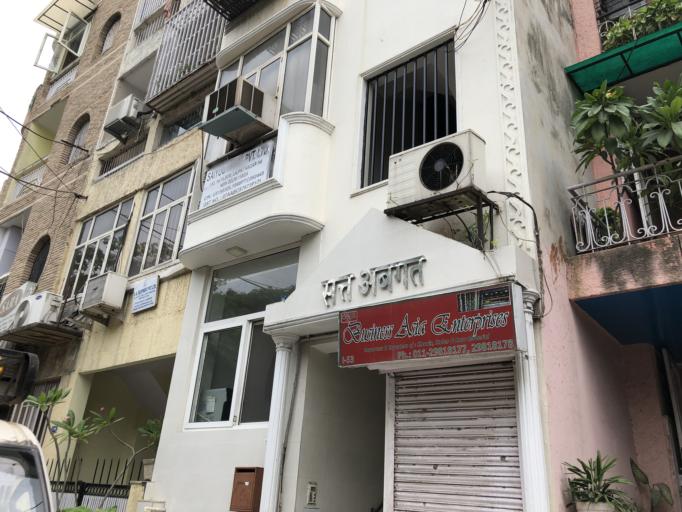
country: IN
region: NCT
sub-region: New Delhi
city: New Delhi
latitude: 28.5787
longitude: 77.2437
